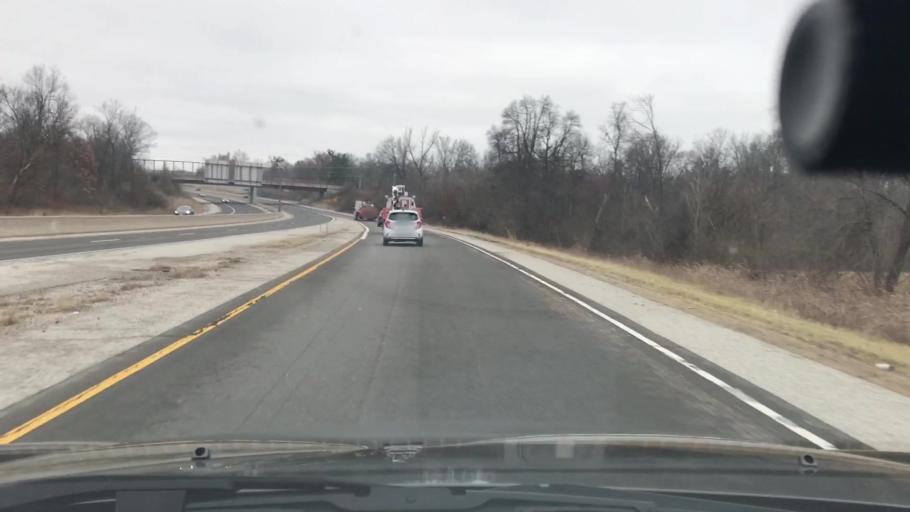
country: US
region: Illinois
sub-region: Madison County
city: Rosewood Heights
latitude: 38.8997
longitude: -90.0659
